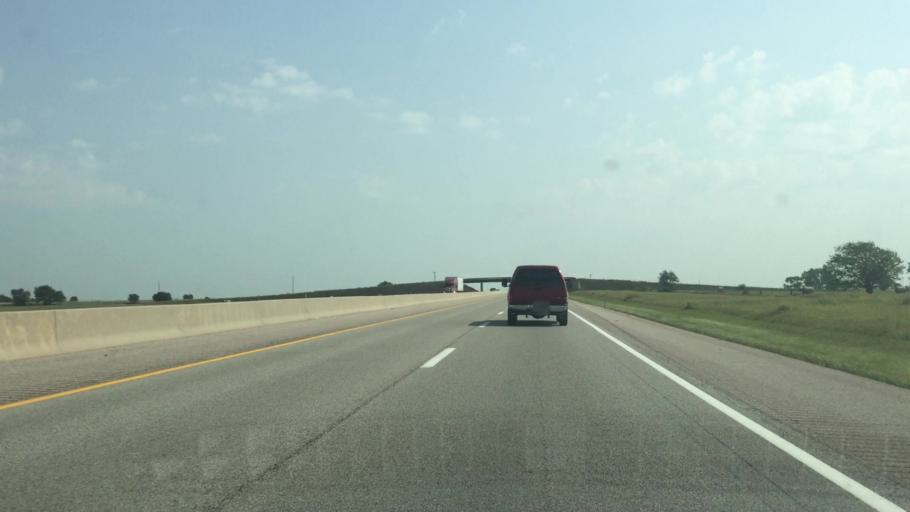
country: US
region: Kansas
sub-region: Butler County
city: El Dorado
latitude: 37.9955
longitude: -96.6956
